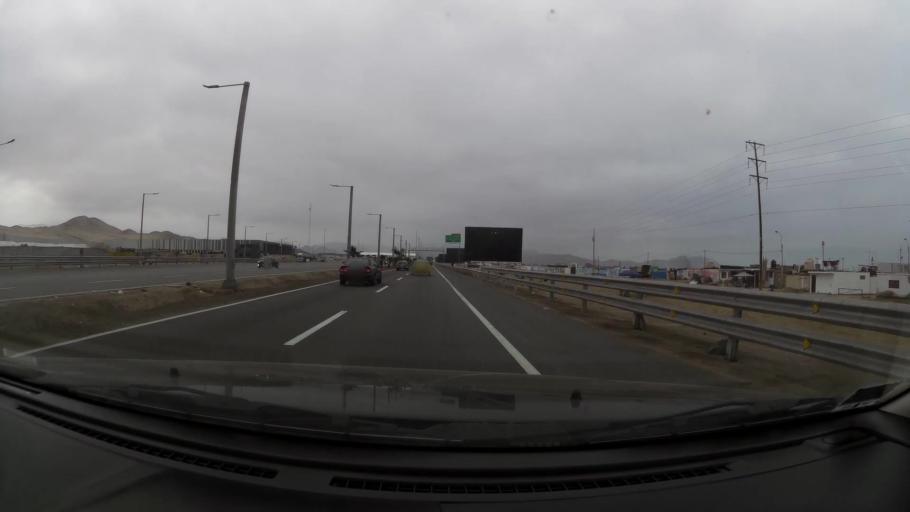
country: PE
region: Lima
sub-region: Lima
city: San Bartolo
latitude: -12.3643
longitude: -76.7921
